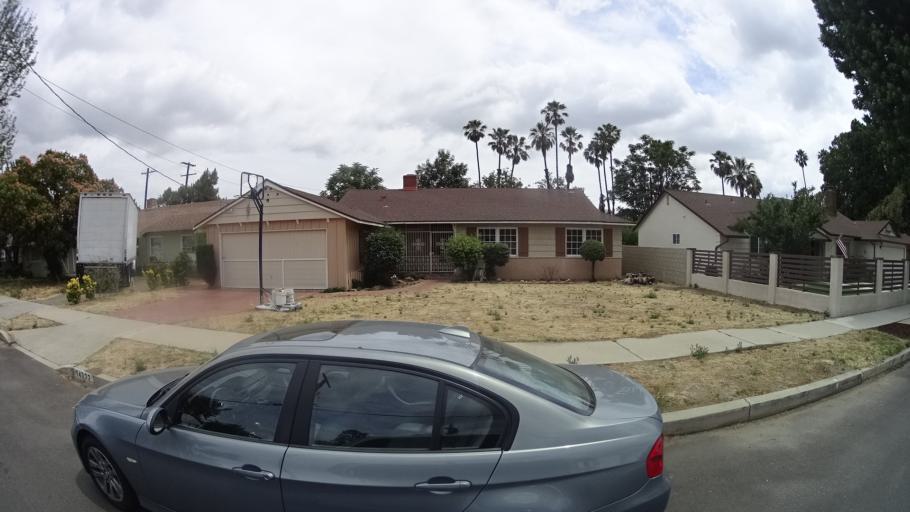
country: US
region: California
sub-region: Los Angeles County
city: San Fernando
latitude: 34.2450
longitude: -118.4578
